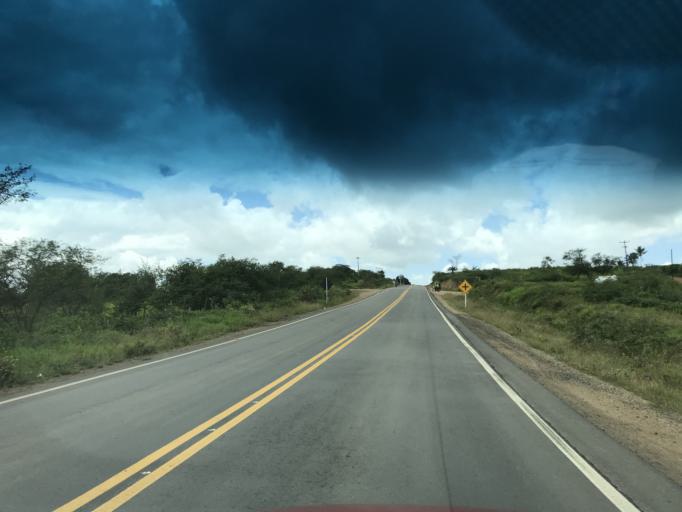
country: BR
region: Bahia
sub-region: Conceicao Do Almeida
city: Conceicao do Almeida
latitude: -12.7110
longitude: -39.2296
